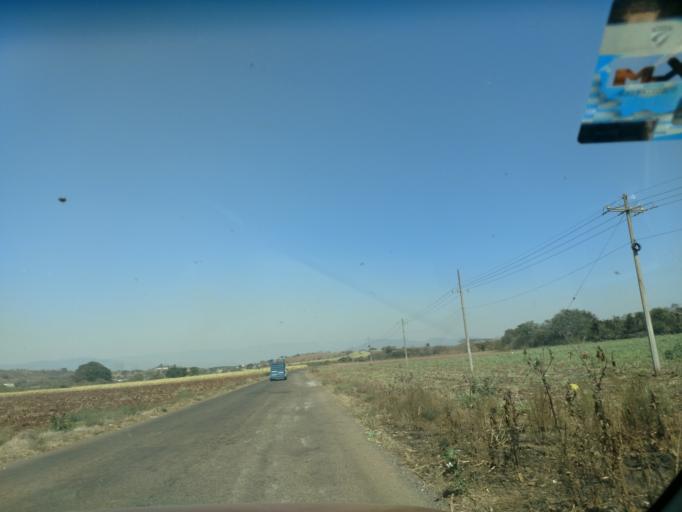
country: MX
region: Nayarit
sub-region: Tepic
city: La Corregidora
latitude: 21.5037
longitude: -104.7245
